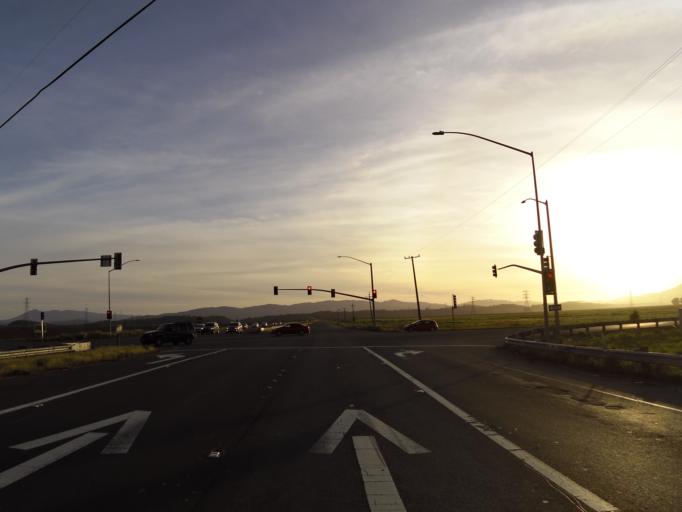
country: US
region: California
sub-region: Marin County
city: Black Point-Green Point
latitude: 38.1344
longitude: -122.4760
